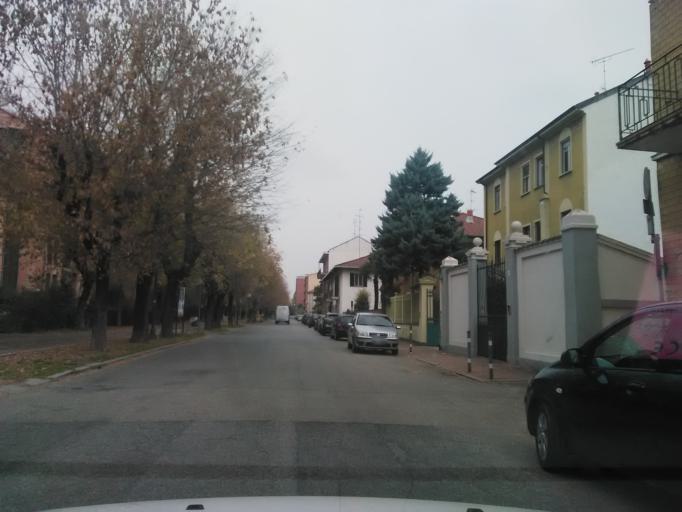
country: IT
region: Piedmont
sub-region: Provincia di Vercelli
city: Vercelli
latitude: 45.3159
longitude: 8.4271
